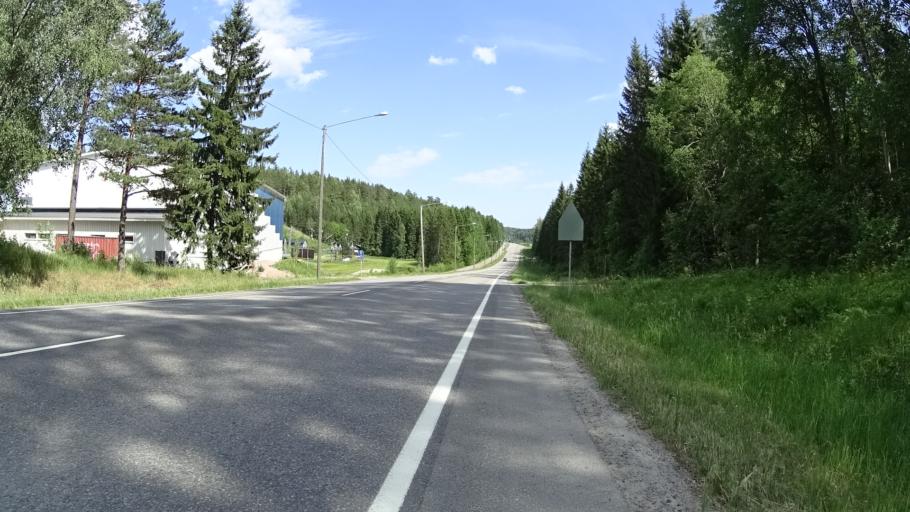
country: FI
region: Uusimaa
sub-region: Raaseporin
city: Karis
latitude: 60.0972
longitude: 23.6005
